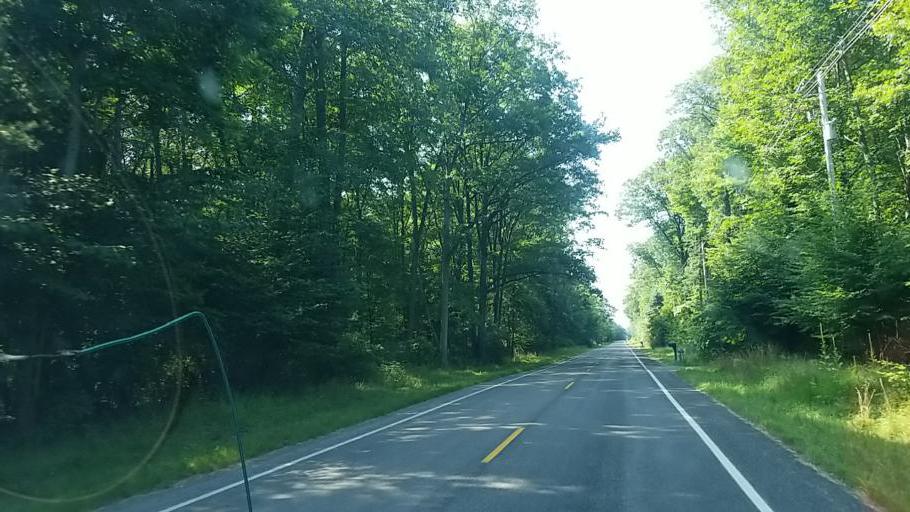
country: US
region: Michigan
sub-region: Muskegon County
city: Whitehall
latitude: 43.3543
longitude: -86.3764
